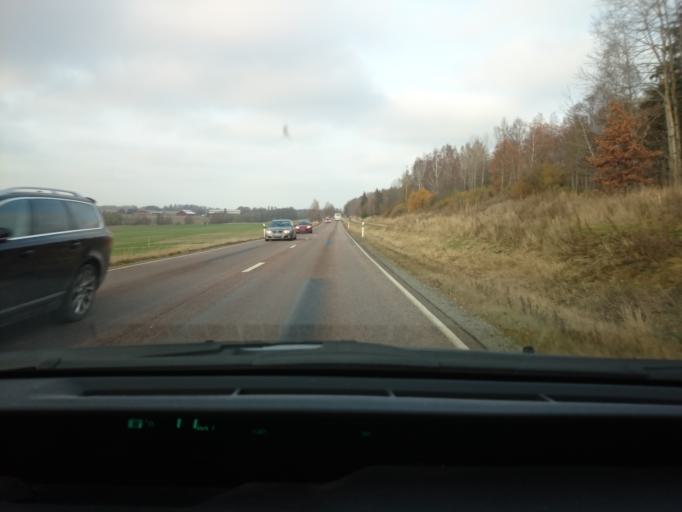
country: SE
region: Vaestmanland
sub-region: Vasteras
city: Skultuna
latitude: 59.6652
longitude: 16.4816
